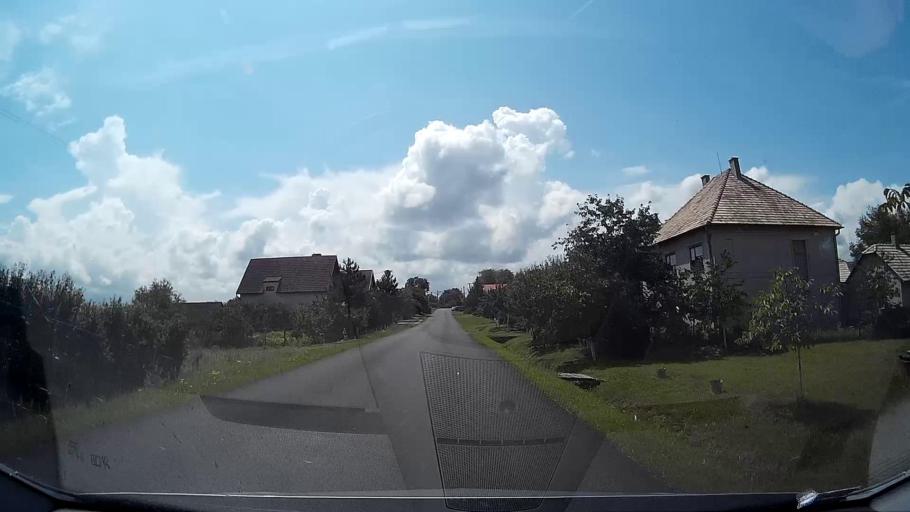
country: SK
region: Banskobystricky
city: Fil'akovo
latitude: 48.3103
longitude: 19.8034
